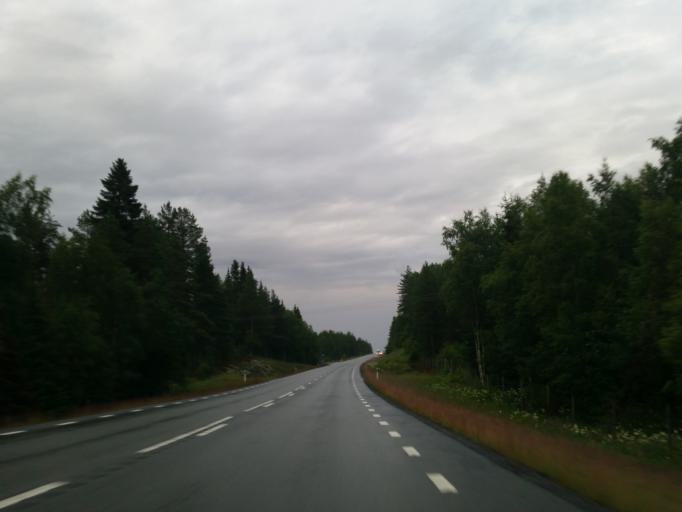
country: SE
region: Vaesterbotten
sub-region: Robertsfors Kommun
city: Robertsfors
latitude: 64.0117
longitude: 20.8153
